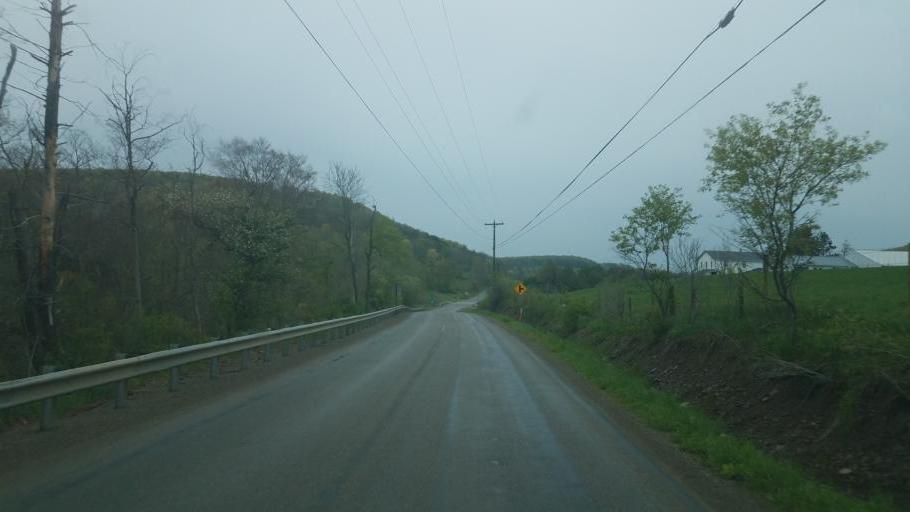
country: US
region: New York
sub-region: Allegany County
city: Andover
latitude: 41.9239
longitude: -77.7845
